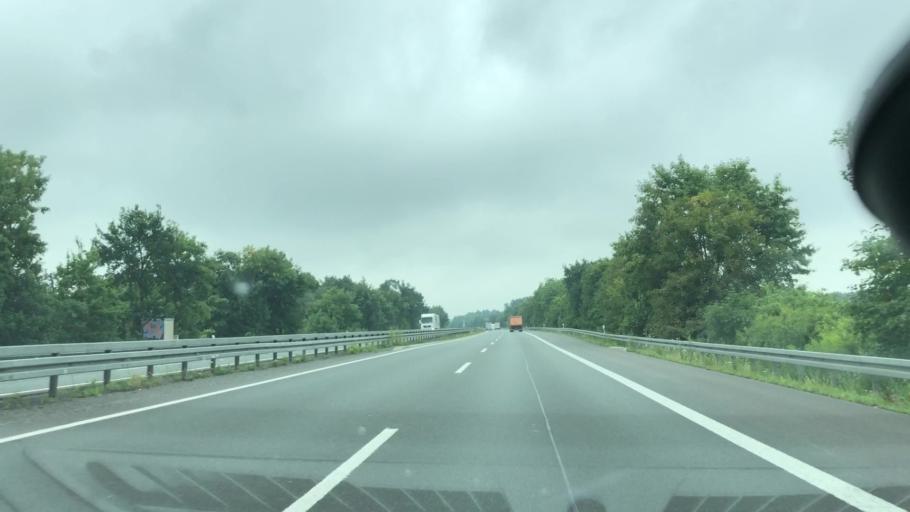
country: DE
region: North Rhine-Westphalia
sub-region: Regierungsbezirk Detmold
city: Hovelhof
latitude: 51.8130
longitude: 8.6999
